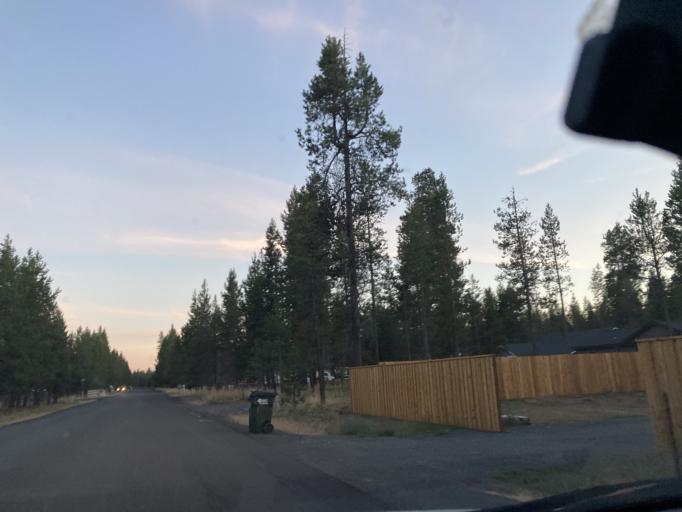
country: US
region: Oregon
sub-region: Deschutes County
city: Three Rivers
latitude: 43.8237
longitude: -121.4656
